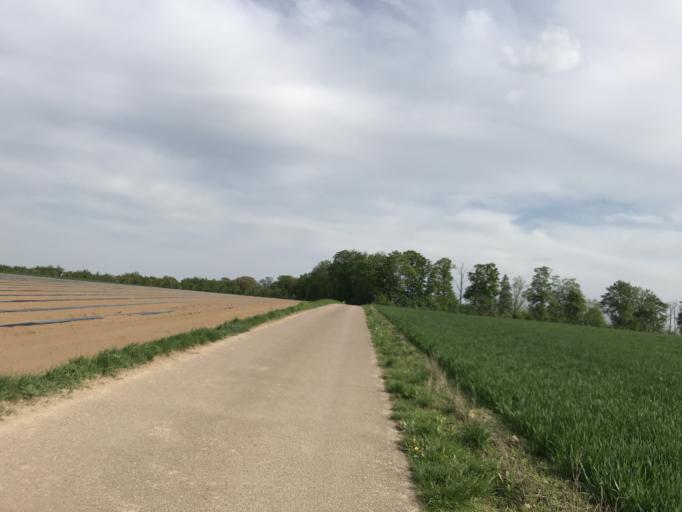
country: DE
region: Rheinland-Pfalz
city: Schwabenheim
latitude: 49.9426
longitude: 8.1039
